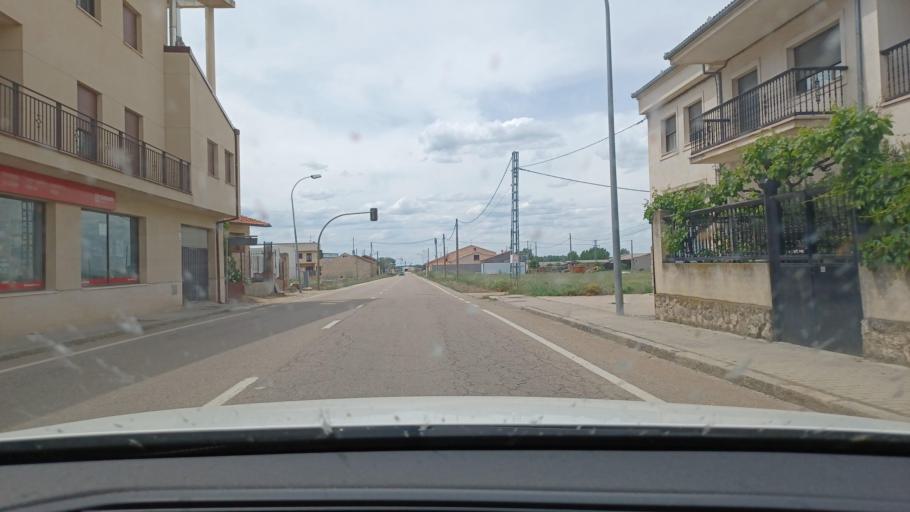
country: ES
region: Castille and Leon
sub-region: Provincia de Segovia
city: Cantalejo
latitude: 41.2611
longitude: -3.9311
